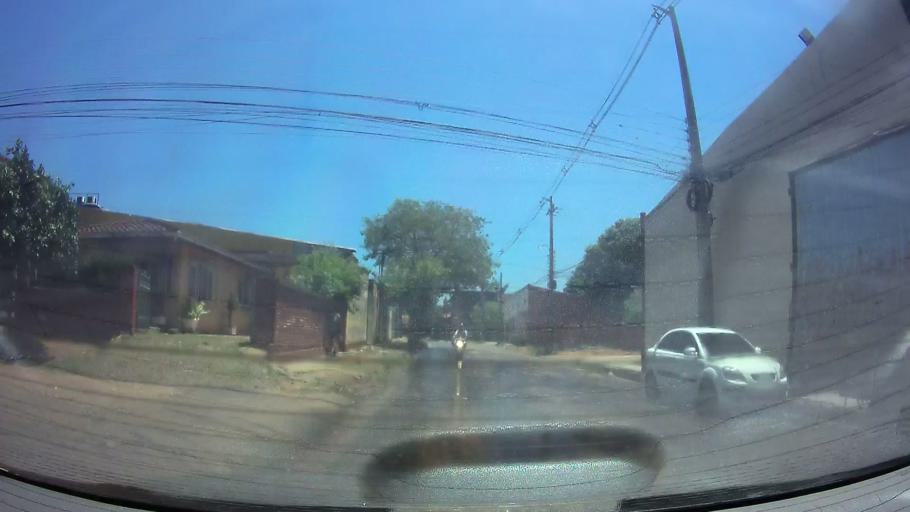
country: PY
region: Central
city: San Lorenzo
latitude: -25.3413
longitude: -57.4885
